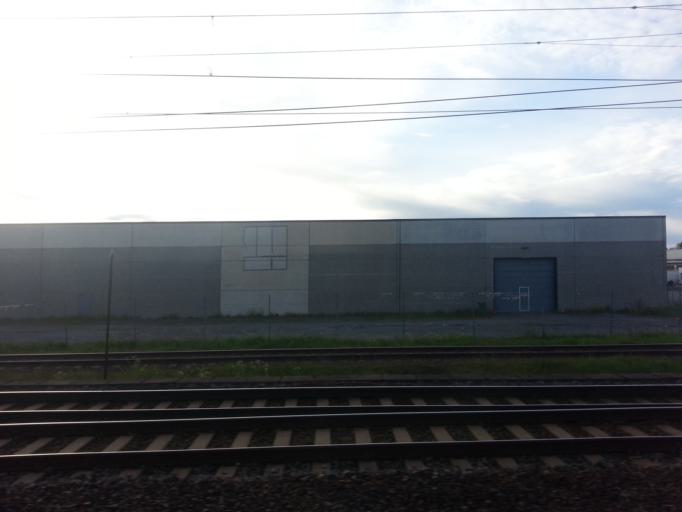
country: NO
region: Akershus
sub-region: Skedsmo
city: Lillestrom
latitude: 59.9668
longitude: 11.0671
